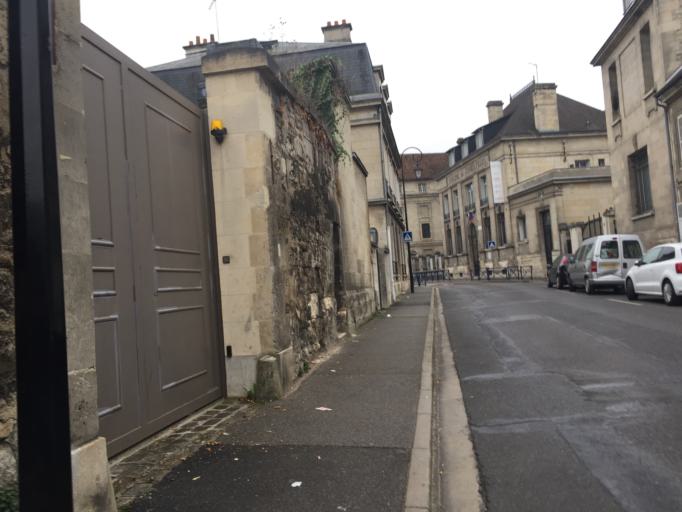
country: FR
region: Picardie
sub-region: Departement de l'Aisne
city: Soissons
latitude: 49.3791
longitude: 3.3243
